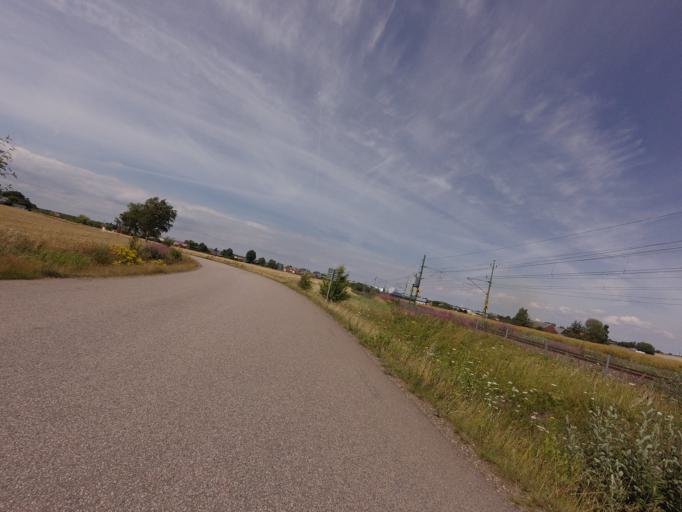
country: SE
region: Skane
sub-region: Helsingborg
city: Rydeback
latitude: 55.9581
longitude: 12.7899
